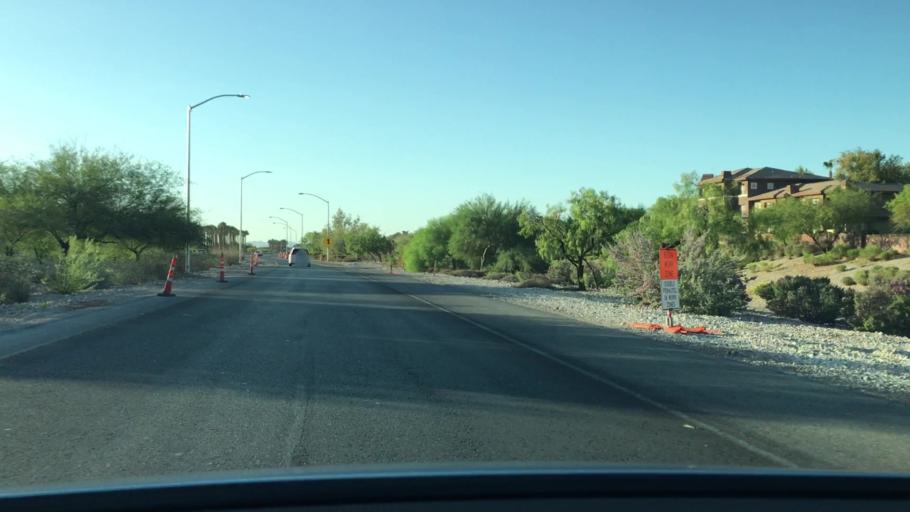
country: US
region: Nevada
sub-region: Clark County
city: Summerlin South
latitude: 36.1852
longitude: -115.3050
